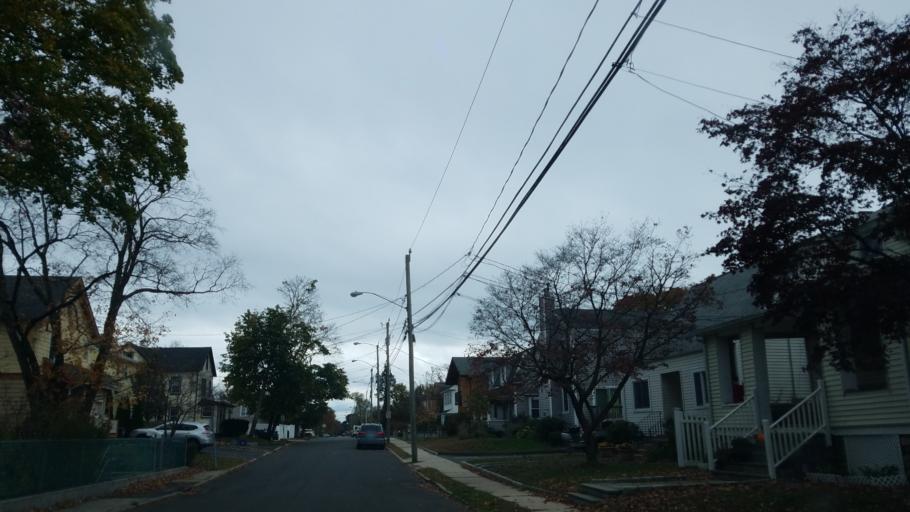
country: US
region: Connecticut
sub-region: Fairfield County
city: Stamford
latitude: 41.0592
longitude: -73.5082
